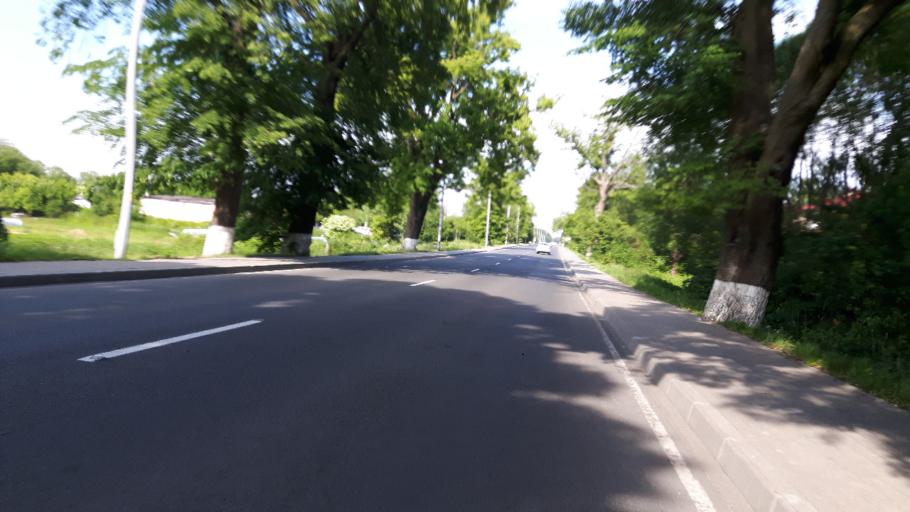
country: RU
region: Kaliningrad
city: Mamonovo
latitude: 54.4634
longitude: 19.9523
